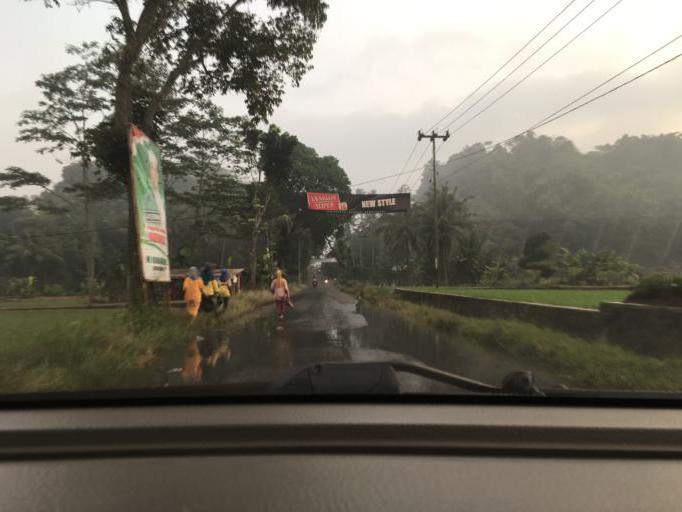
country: ID
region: West Java
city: Pasireurih
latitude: -7.1813
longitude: 108.1970
